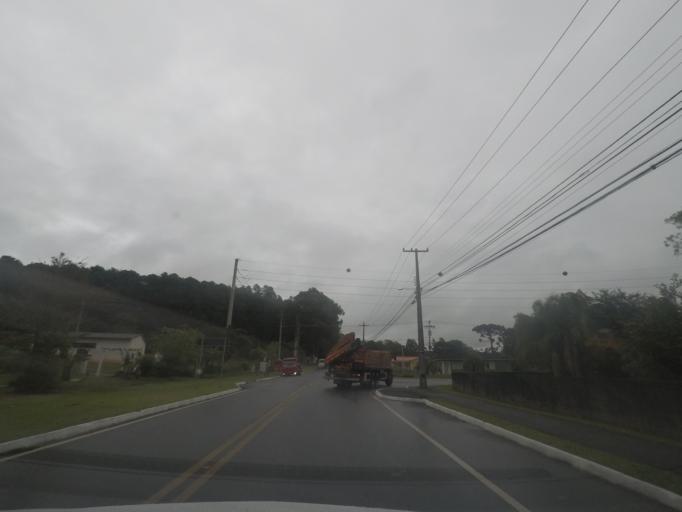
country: BR
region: Parana
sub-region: Quatro Barras
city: Quatro Barras
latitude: -25.3816
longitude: -49.1282
